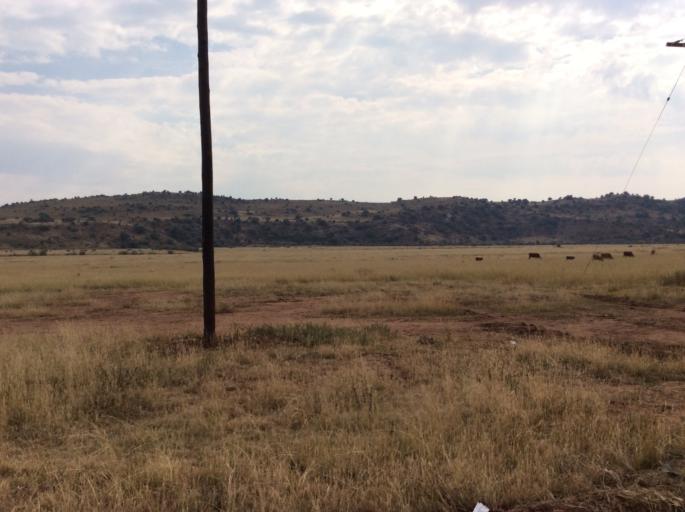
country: LS
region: Mafeteng
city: Mafeteng
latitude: -29.9858
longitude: 27.0005
